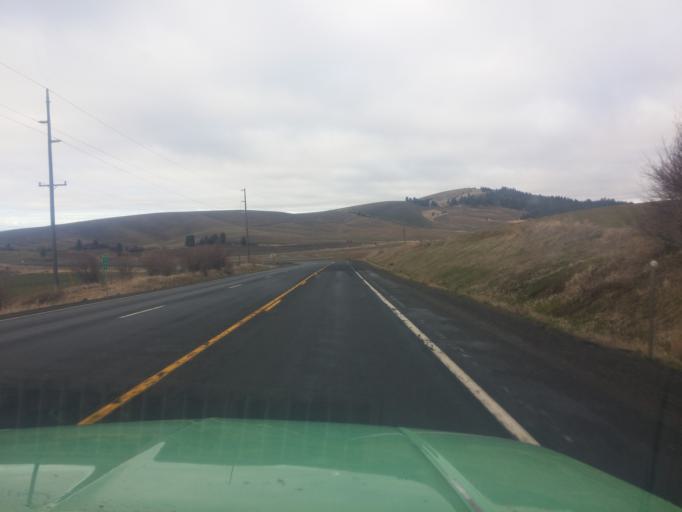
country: US
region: Idaho
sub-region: Latah County
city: Moscow
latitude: 46.8602
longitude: -117.0179
